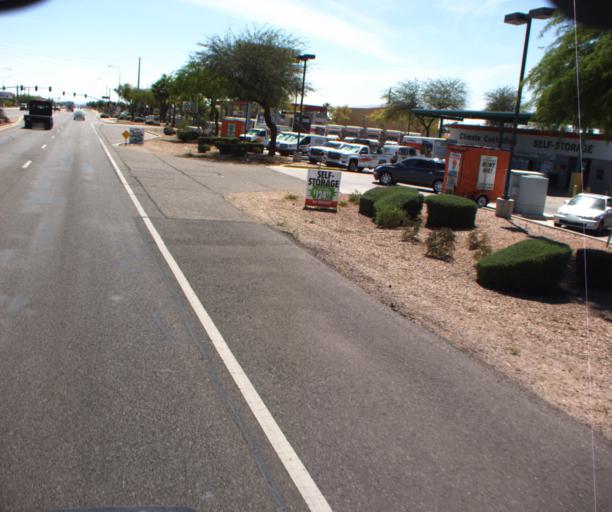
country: US
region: Arizona
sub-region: Maricopa County
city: Sun Lakes
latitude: 33.2204
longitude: -111.8413
